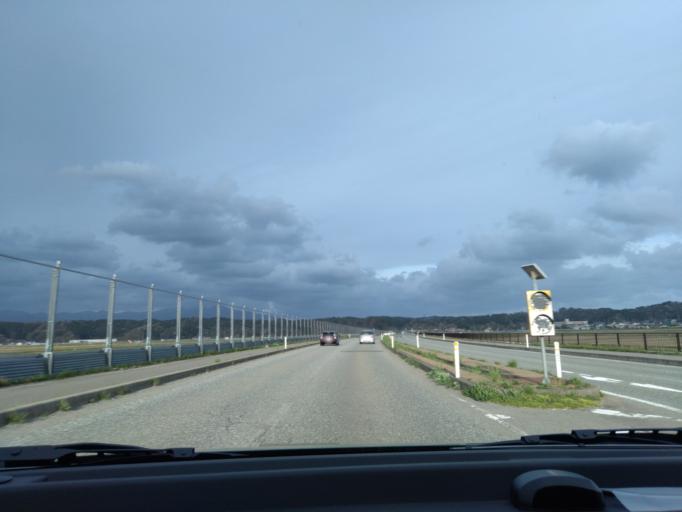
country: JP
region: Akita
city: Akita Shi
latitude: 39.7542
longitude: 140.1008
